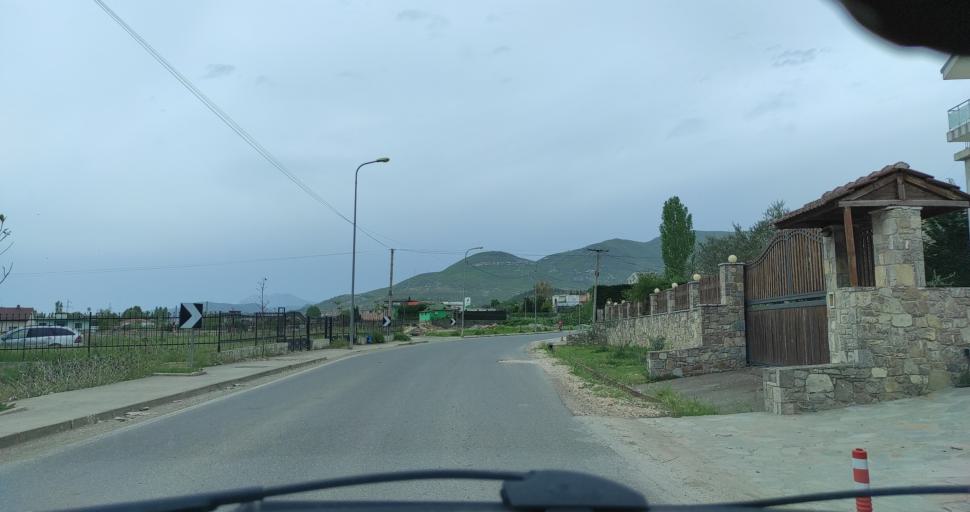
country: AL
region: Lezhe
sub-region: Rrethi i Kurbinit
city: Lac
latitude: 41.6252
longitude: 19.7090
